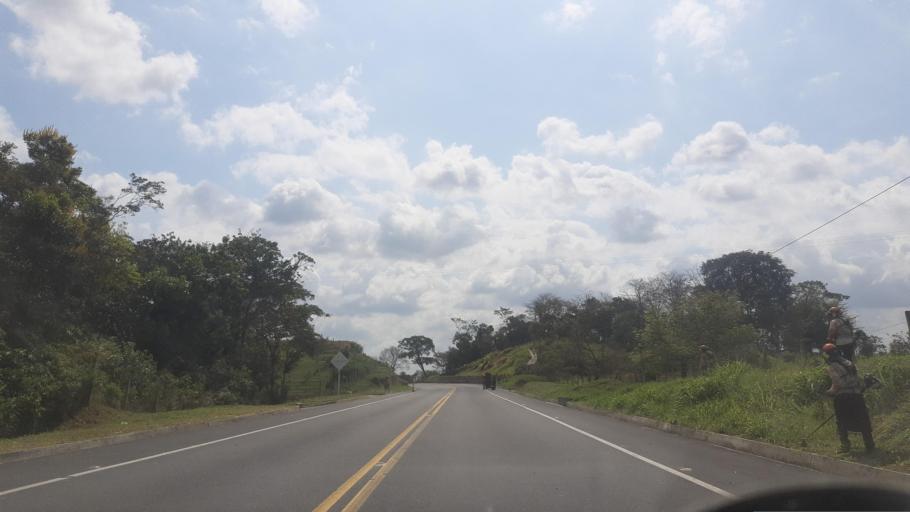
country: CO
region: Casanare
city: Monterrey
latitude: 4.8308
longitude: -72.8182
